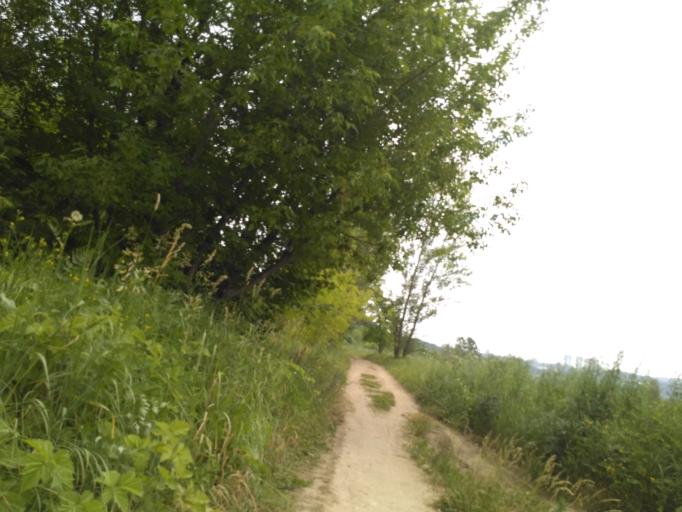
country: RU
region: Nizjnij Novgorod
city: Nizhniy Novgorod
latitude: 56.2747
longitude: 43.9713
